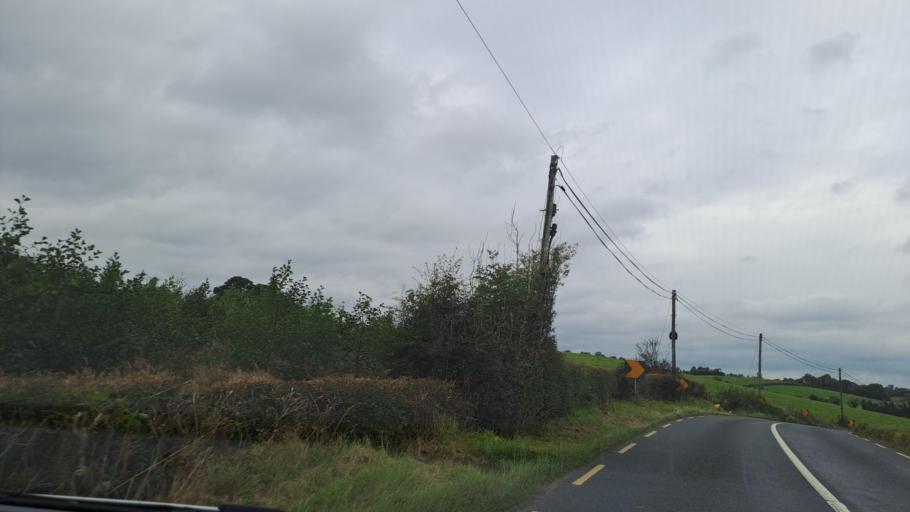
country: IE
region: Ulster
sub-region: An Cabhan
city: Bailieborough
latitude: 53.9324
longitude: -6.9655
